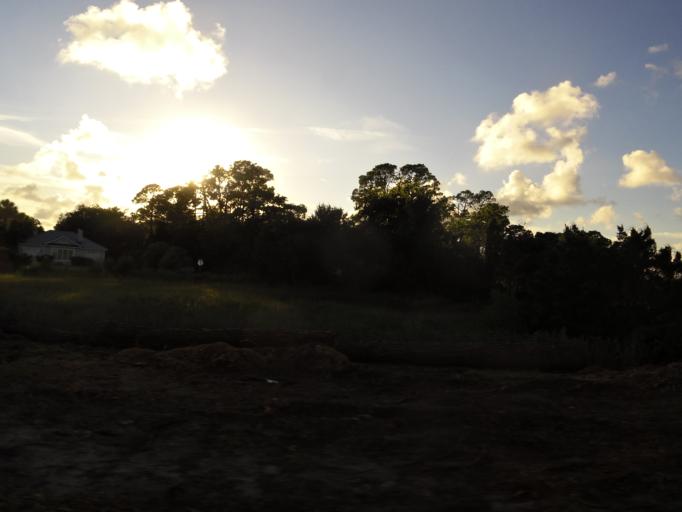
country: US
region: Georgia
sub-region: Glynn County
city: Brunswick
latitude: 31.1463
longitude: -81.4778
